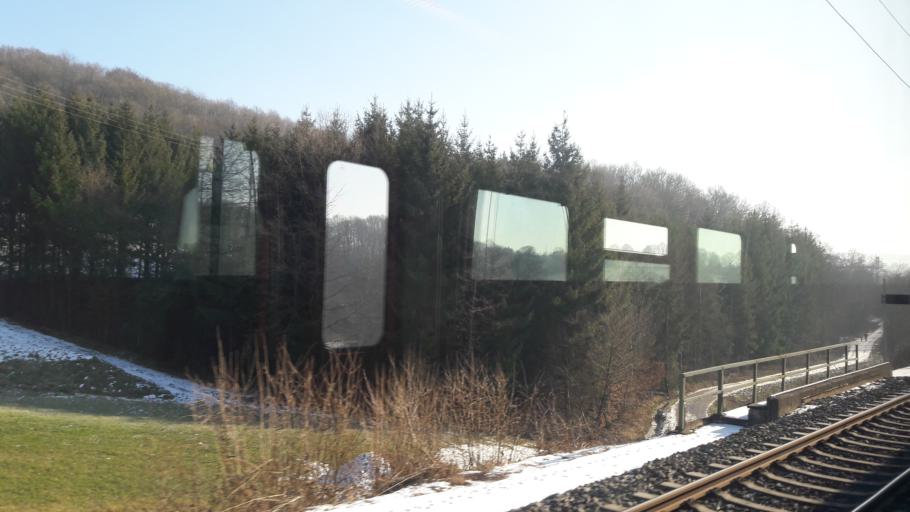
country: DE
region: Saarland
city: Sankt Wendel
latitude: 49.4862
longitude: 7.1711
